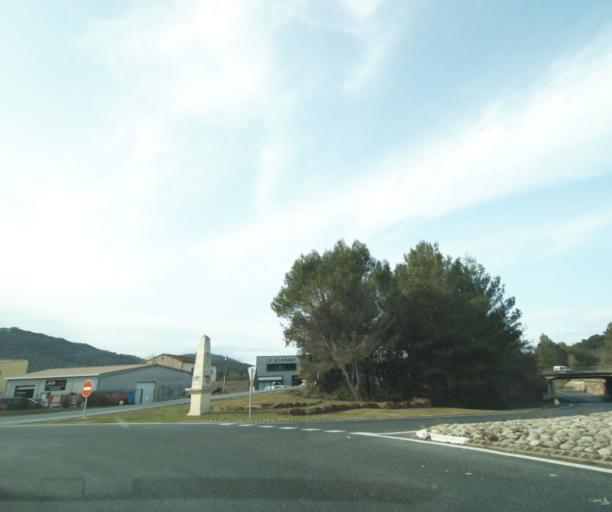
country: FR
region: Provence-Alpes-Cote d'Azur
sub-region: Departement du Var
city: Tourves
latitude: 43.4053
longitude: 5.9382
